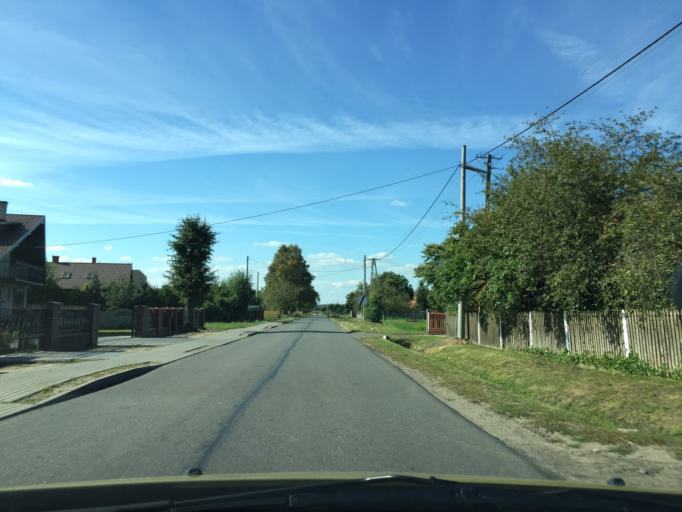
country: PL
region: Greater Poland Voivodeship
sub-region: Powiat kaliski
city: Stawiszyn
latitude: 51.9450
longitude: 18.1853
